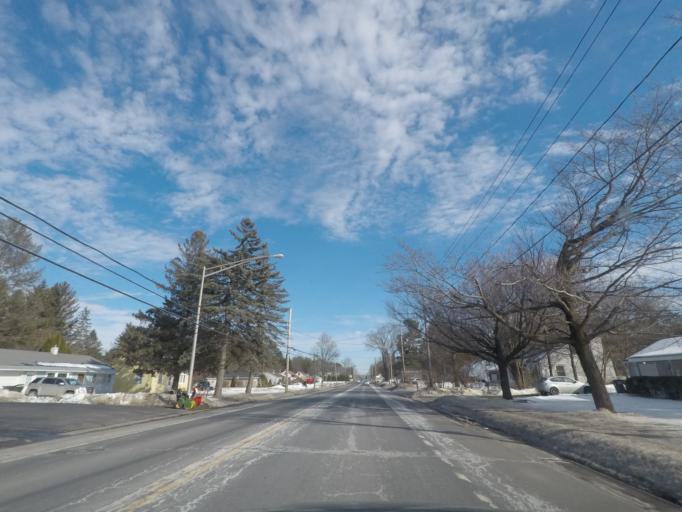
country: US
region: New York
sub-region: Schenectady County
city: Rotterdam
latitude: 42.7878
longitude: -74.0070
